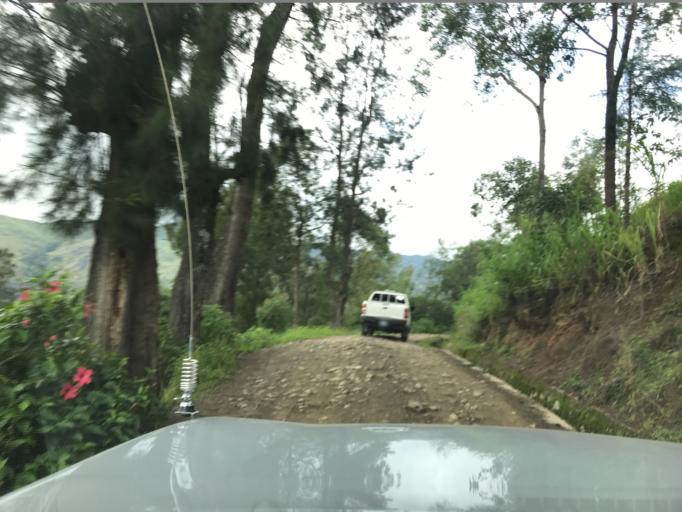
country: TL
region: Aileu
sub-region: Aileu Villa
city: Aileu
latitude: -8.8524
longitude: 125.5852
